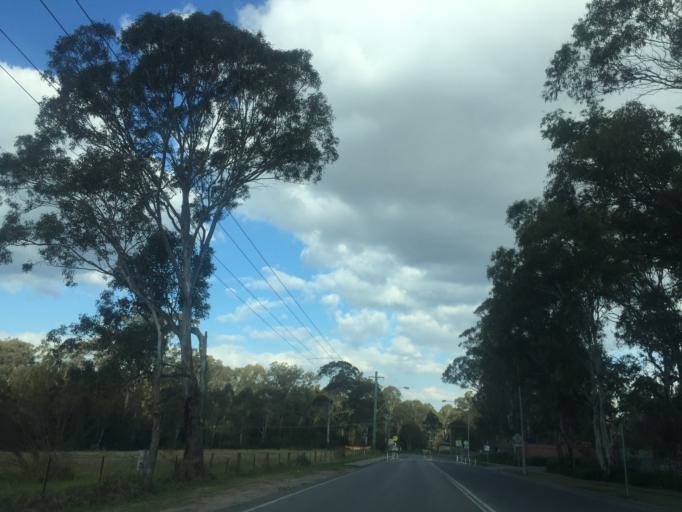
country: AU
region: New South Wales
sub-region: Blacktown
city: Rouse Hill
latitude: -33.6840
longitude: 150.9093
